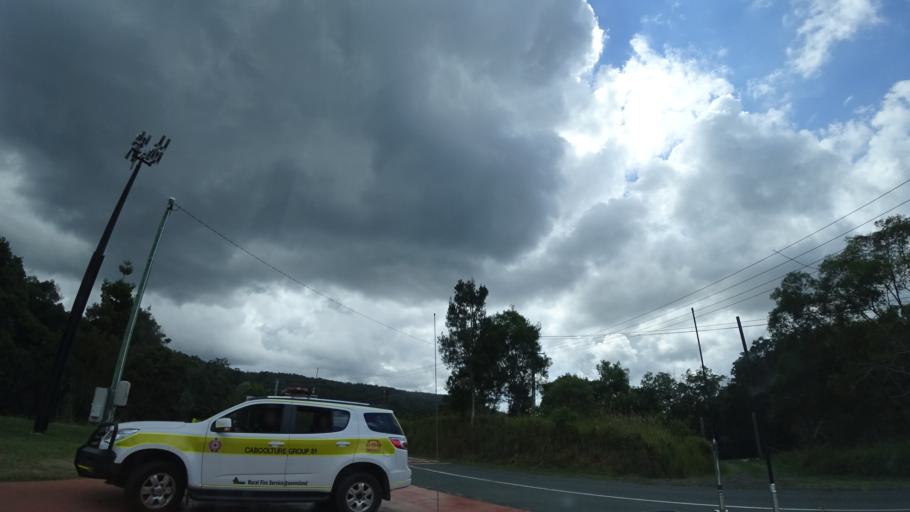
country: AU
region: Queensland
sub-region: Moreton Bay
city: Highvale
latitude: -27.3956
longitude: 152.7823
